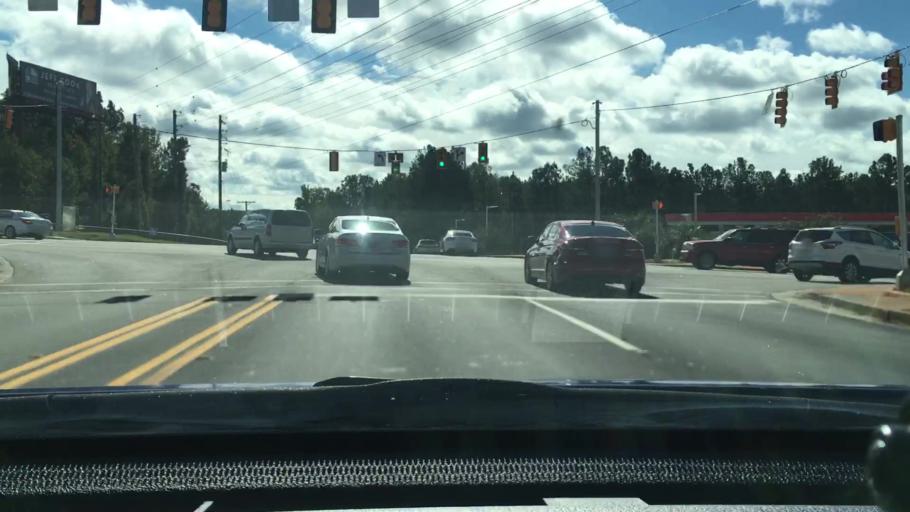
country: US
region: South Carolina
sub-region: Lexington County
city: Seven Oaks
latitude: 34.0669
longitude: -81.1457
